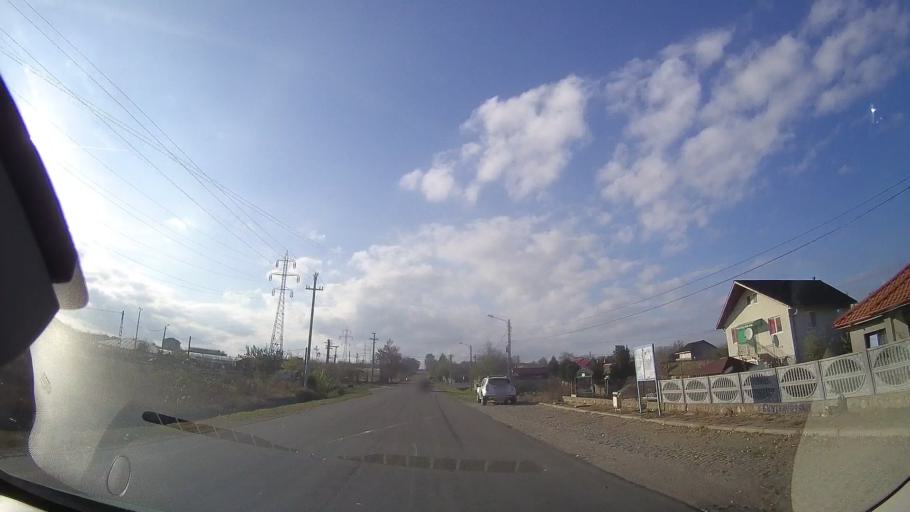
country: RO
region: Constanta
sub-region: Comuna Limanu
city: Limanu
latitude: 43.7940
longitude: 28.5343
